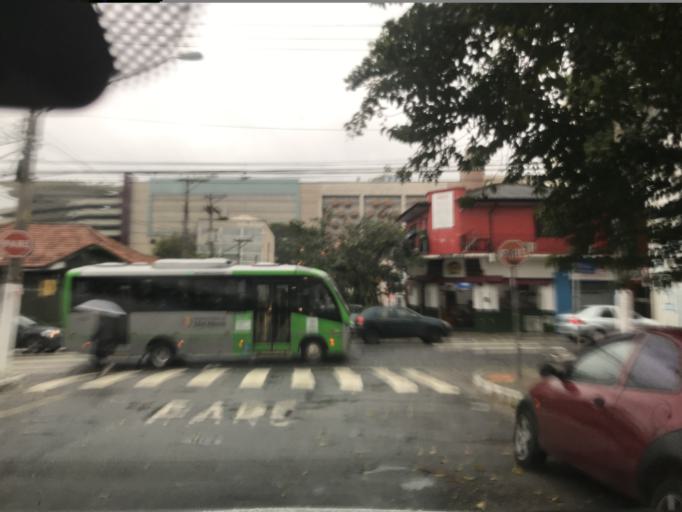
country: BR
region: Sao Paulo
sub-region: Sao Paulo
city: Sao Paulo
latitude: -23.5283
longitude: -46.6822
